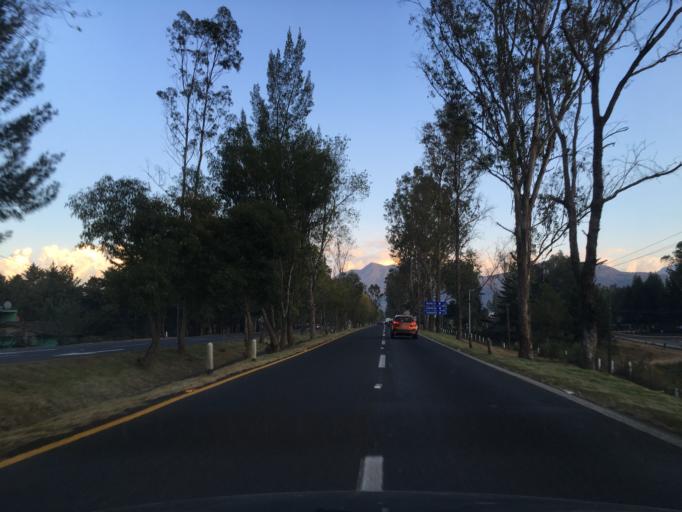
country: MX
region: Michoacan
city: Patzcuaro
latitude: 19.5436
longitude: -101.5849
